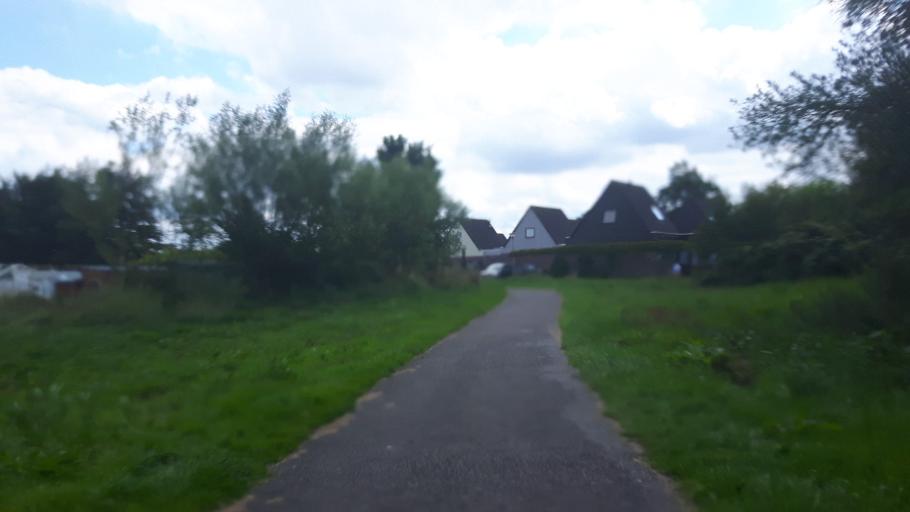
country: NL
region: South Holland
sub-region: Gemeente Krimpen aan den IJssel
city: Krimpen aan den IJssel
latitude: 51.9021
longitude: 4.6334
